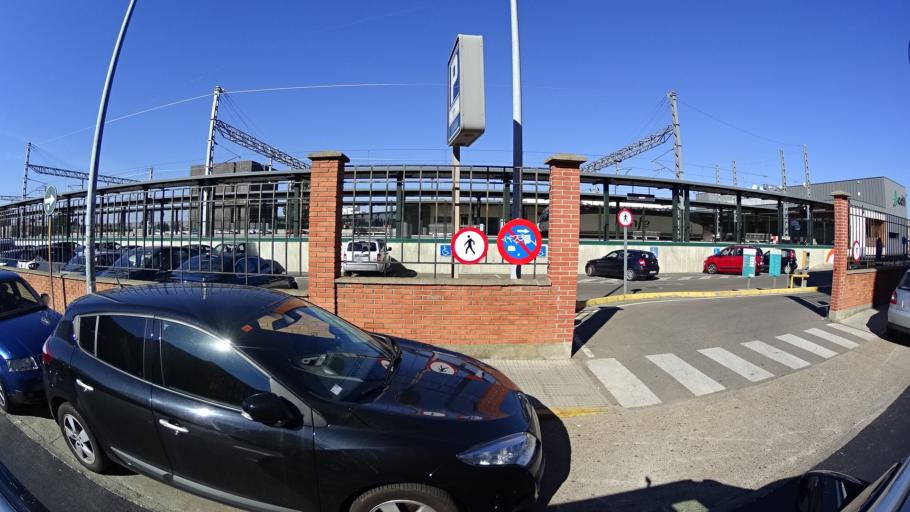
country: ES
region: Castille and Leon
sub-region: Provincia de Leon
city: Leon
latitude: 42.5950
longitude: -5.5807
